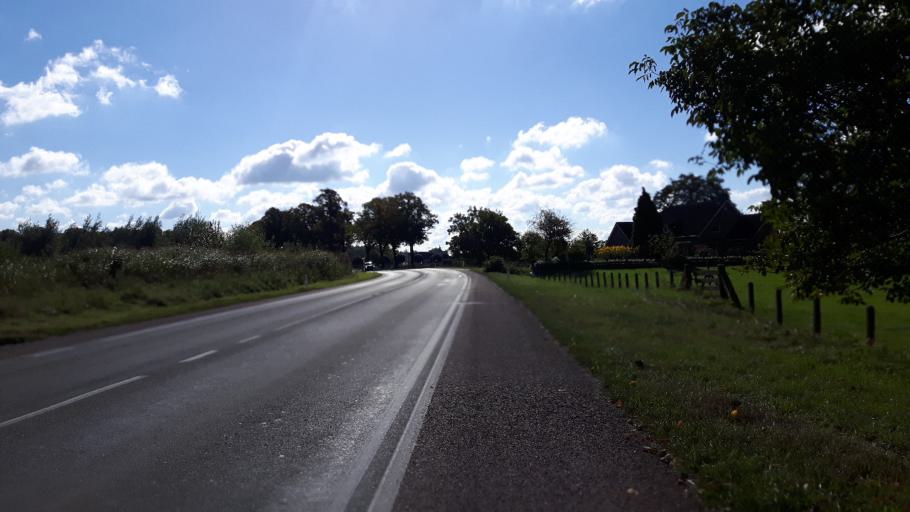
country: NL
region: Gelderland
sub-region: Gemeente Culemborg
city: Culemborg
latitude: 51.9419
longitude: 5.2462
